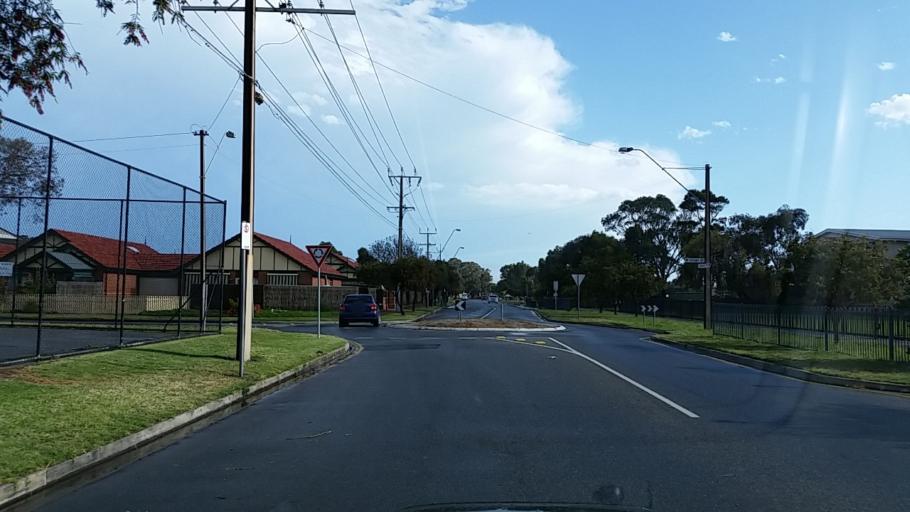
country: AU
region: South Australia
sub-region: Charles Sturt
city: Henley Beach
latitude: -34.9226
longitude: 138.5014
